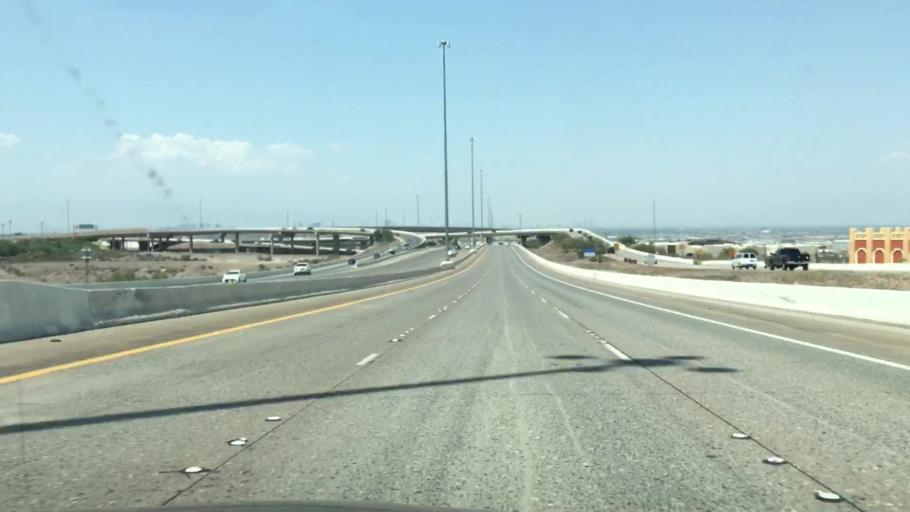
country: US
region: Nevada
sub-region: Clark County
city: Henderson
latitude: 36.0297
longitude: -115.0098
